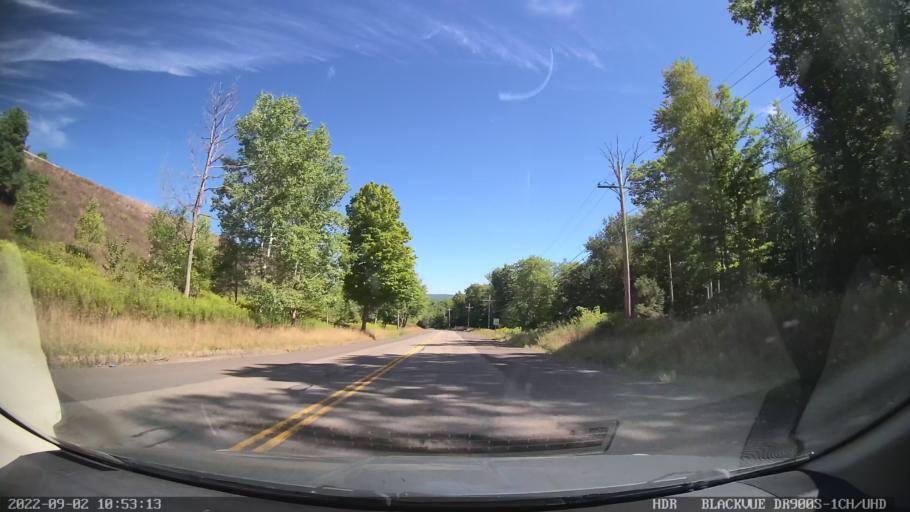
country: US
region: Pennsylvania
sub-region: Tioga County
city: Blossburg
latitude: 41.6432
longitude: -77.0989
